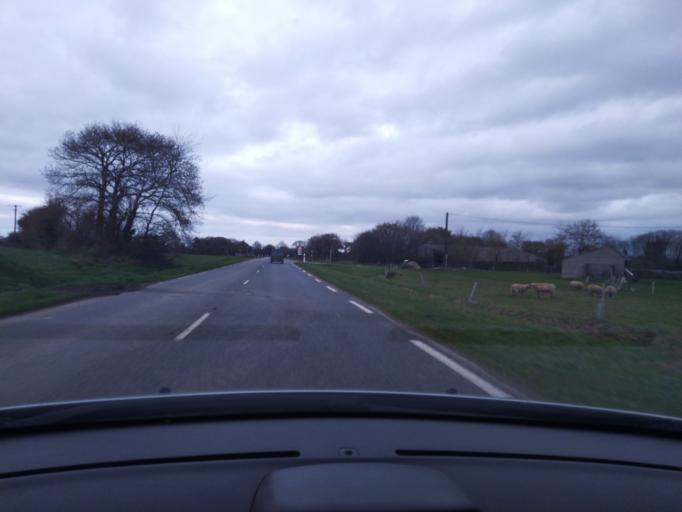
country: FR
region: Brittany
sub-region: Departement des Cotes-d'Armor
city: Plouaret
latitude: 48.5997
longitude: -3.4904
